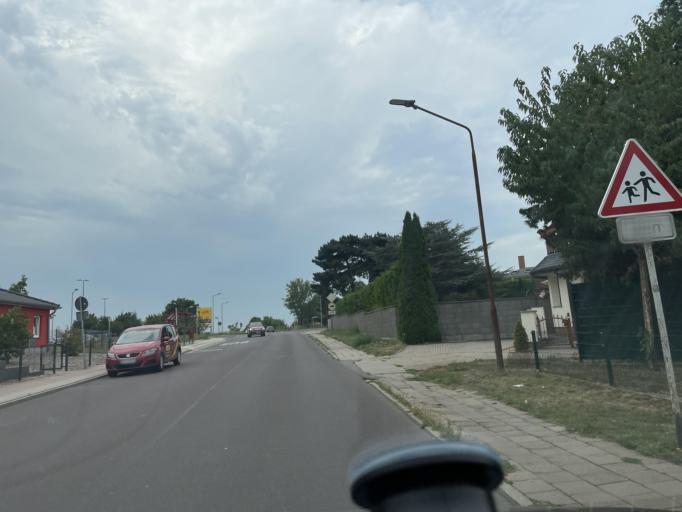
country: DE
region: Saxony-Anhalt
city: Calbe
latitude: 51.9030
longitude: 11.7661
